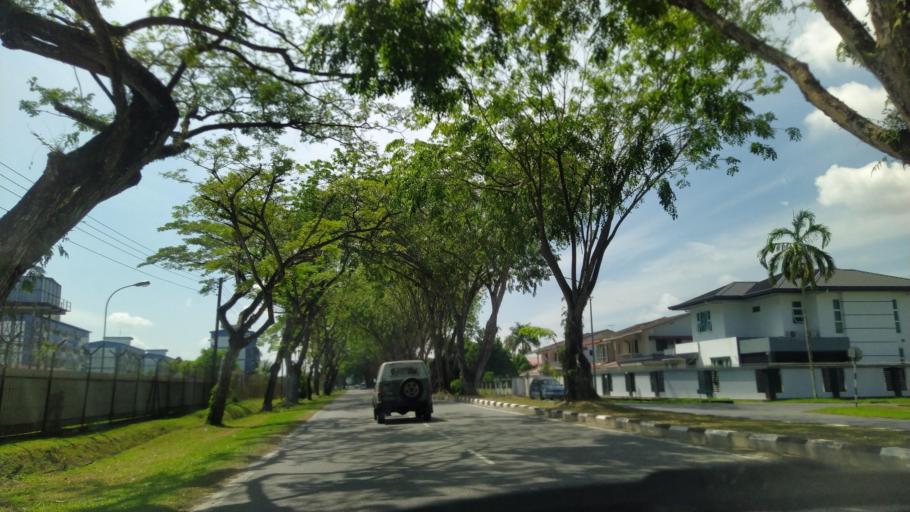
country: MY
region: Sarawak
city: Sibu
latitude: 2.3125
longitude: 111.8318
